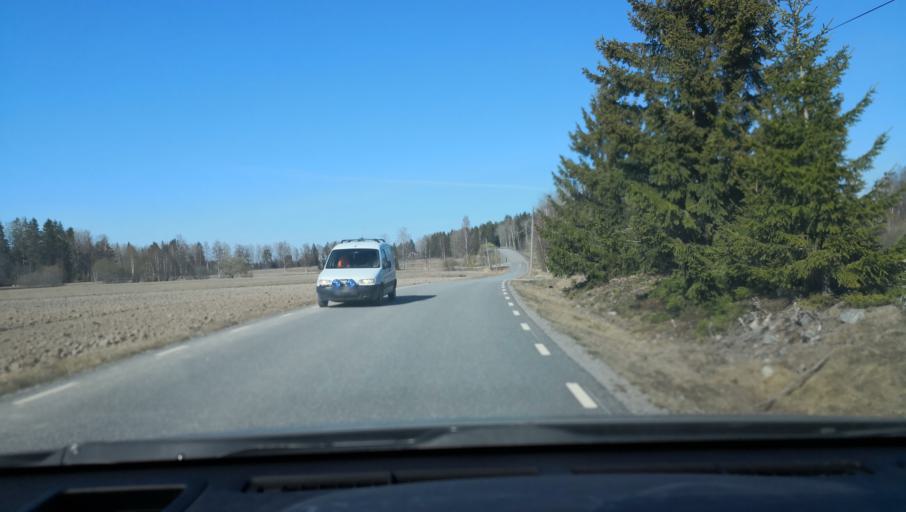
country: SE
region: Vaestmanland
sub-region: Sala Kommun
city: Sala
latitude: 59.9677
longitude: 16.4622
